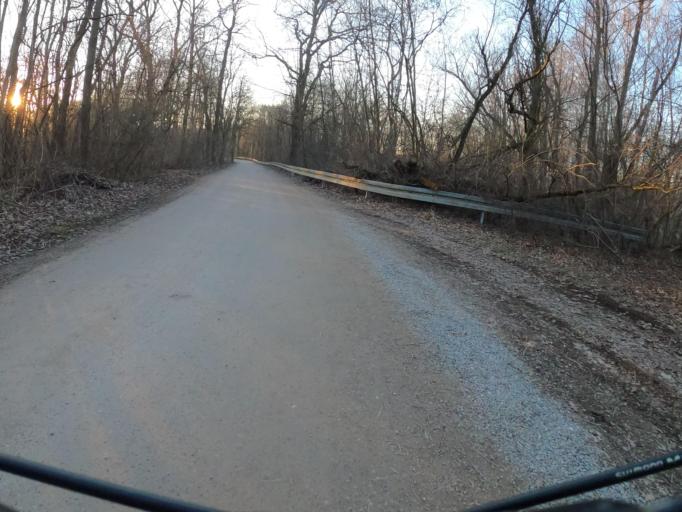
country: DE
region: Bavaria
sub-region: Swabia
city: Nersingen
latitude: 48.4352
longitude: 10.1169
